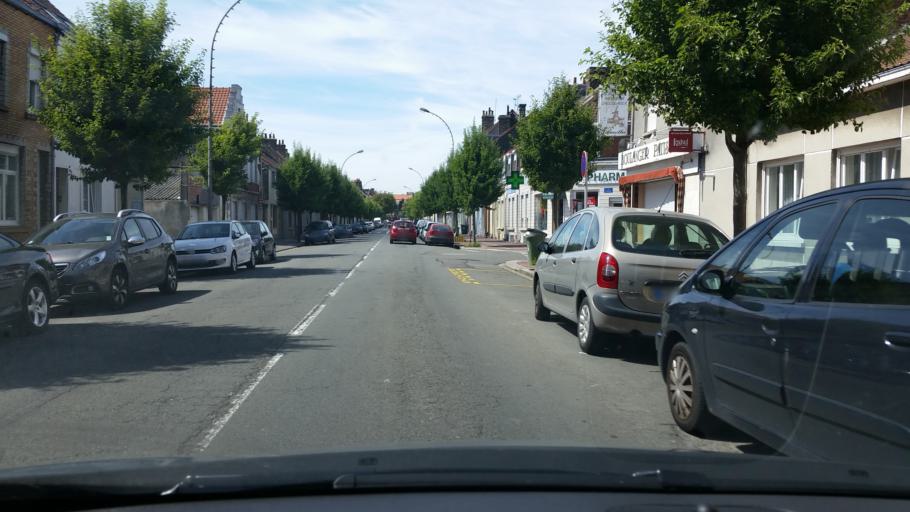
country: FR
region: Nord-Pas-de-Calais
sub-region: Departement du Pas-de-Calais
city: Calais
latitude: 50.9436
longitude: 1.8710
